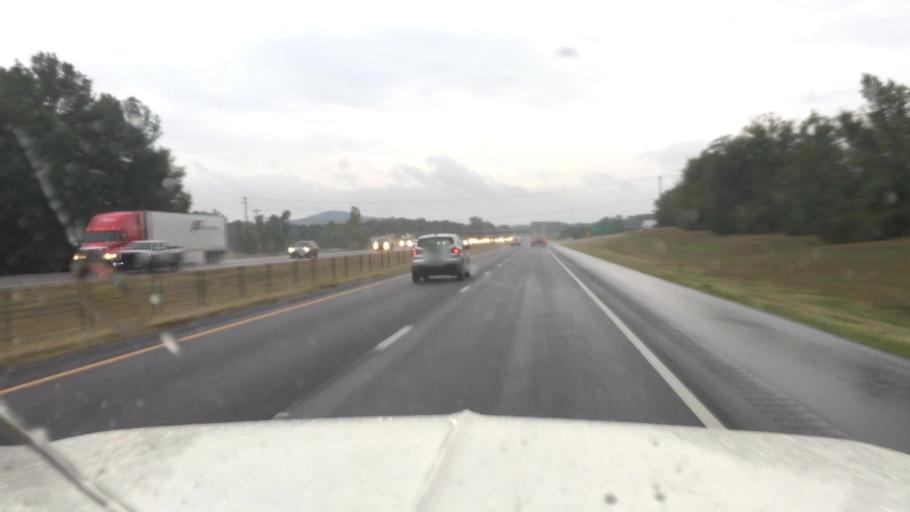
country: US
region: Alabama
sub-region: Morgan County
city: Hartselle
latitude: 34.4181
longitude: -86.8988
